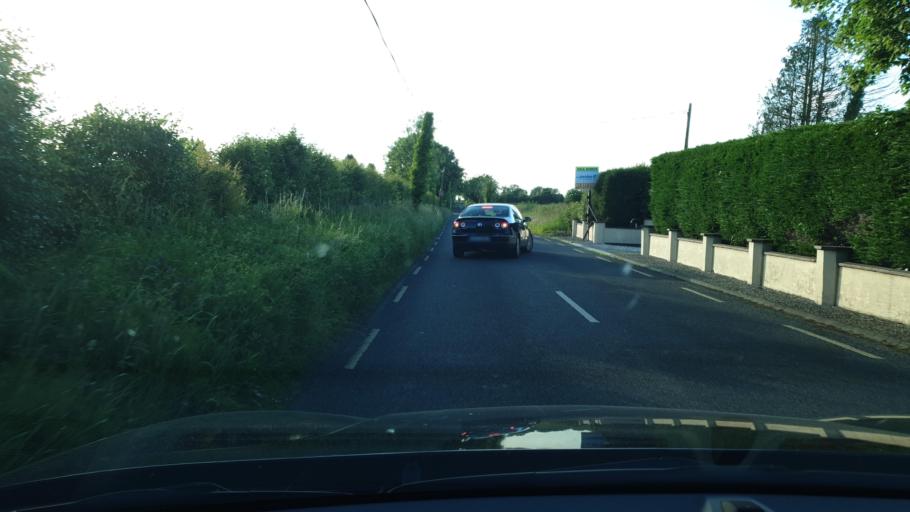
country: IE
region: Leinster
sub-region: An Mhi
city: Ashbourne
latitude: 53.4757
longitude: -6.4254
